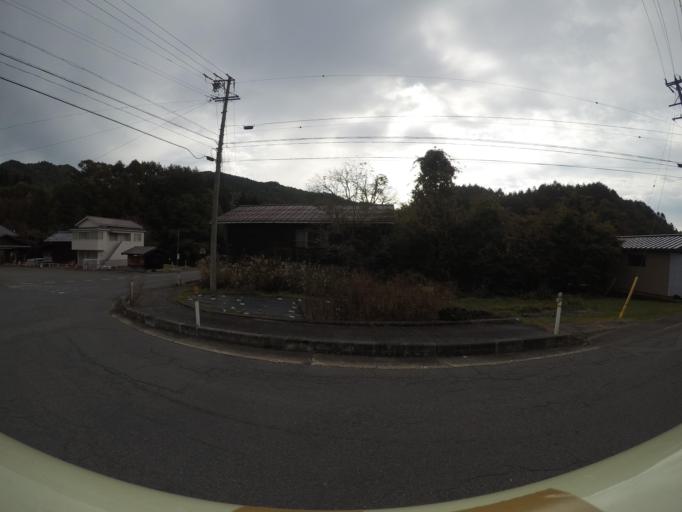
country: JP
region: Nagano
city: Ina
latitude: 35.9400
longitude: 137.6000
